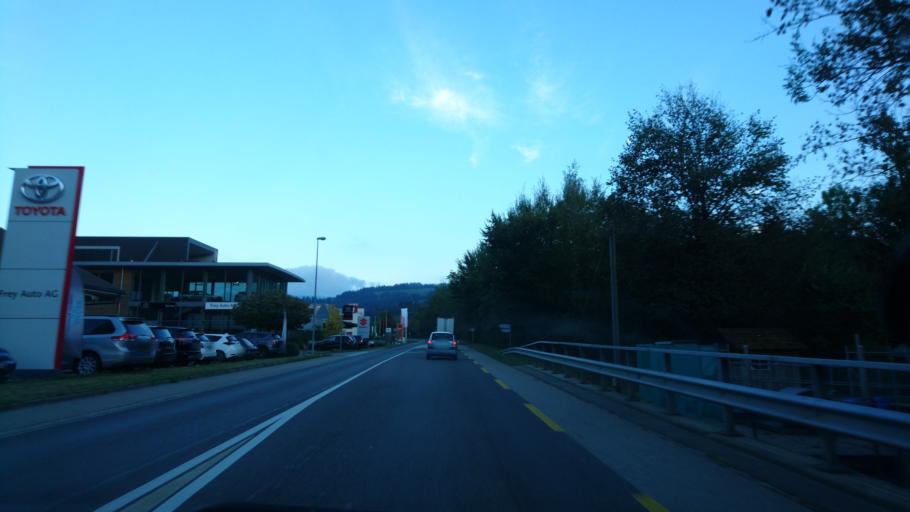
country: CH
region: Bern
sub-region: Emmental District
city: Trubschachen
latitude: 46.9257
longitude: 7.8161
